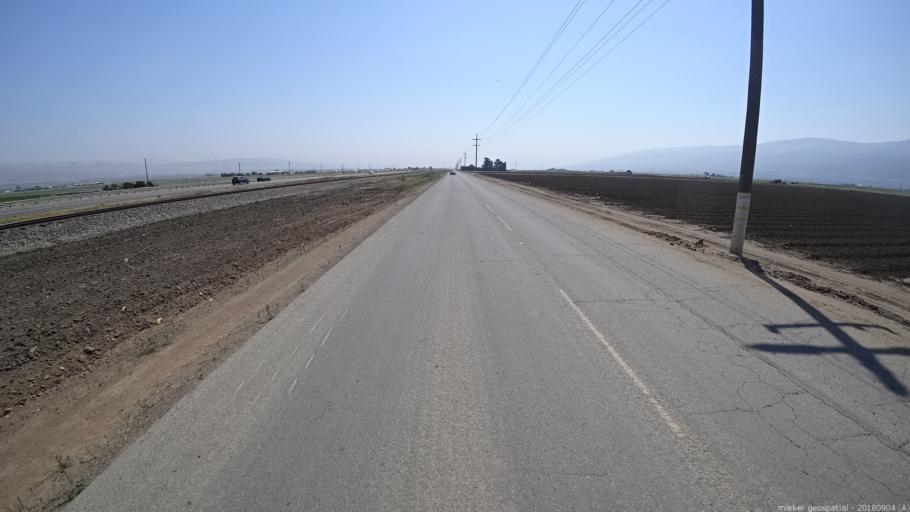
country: US
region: California
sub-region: Monterey County
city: Gonzales
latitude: 36.5337
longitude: -121.4788
